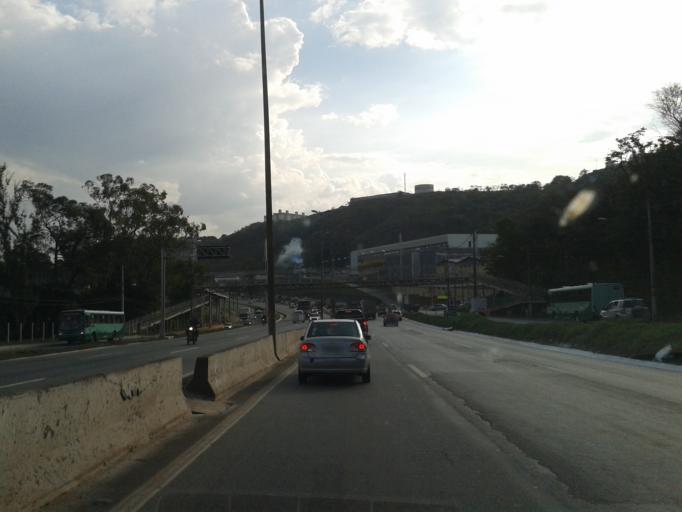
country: BR
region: Minas Gerais
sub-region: Belo Horizonte
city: Belo Horizonte
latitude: -19.8918
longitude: -43.9758
